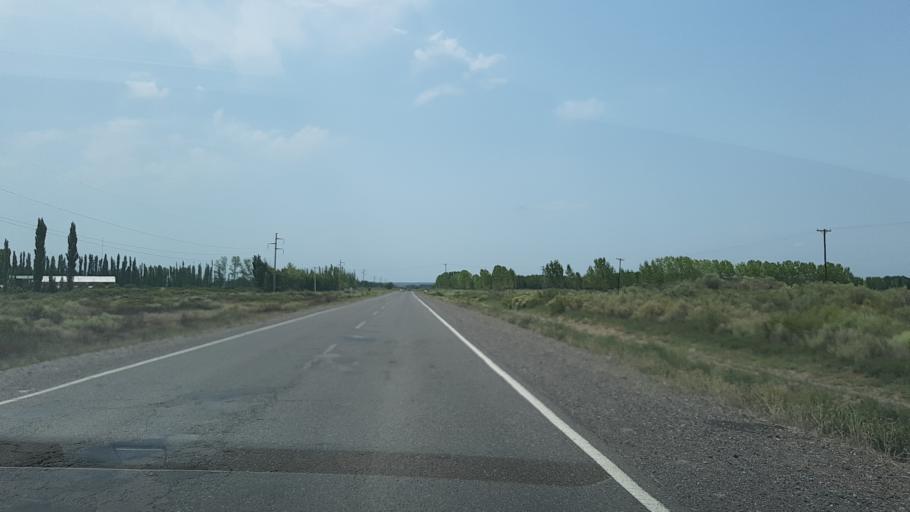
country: AR
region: Rio Negro
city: Catriel
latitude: -37.9172
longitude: -67.8714
